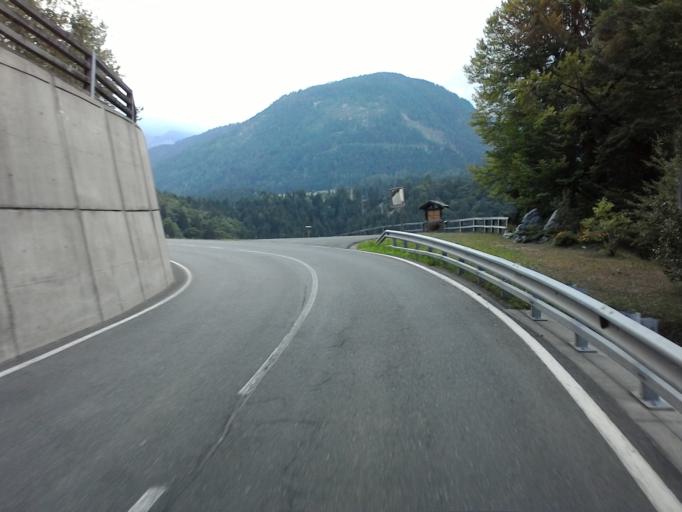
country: AT
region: Carinthia
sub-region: Politischer Bezirk Spittal an der Drau
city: Oberdrauburg
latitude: 46.6822
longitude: 12.9489
